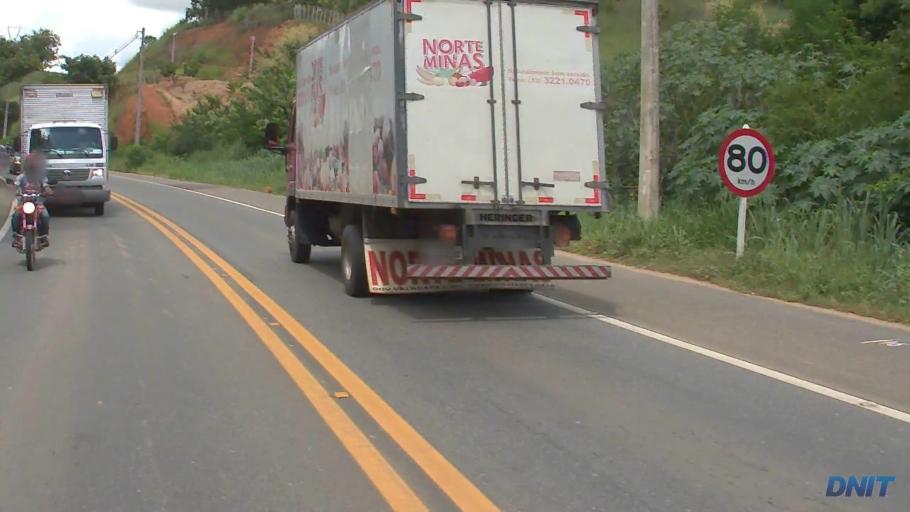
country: BR
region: Minas Gerais
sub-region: Governador Valadares
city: Governador Valadares
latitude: -18.8700
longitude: -41.9910
